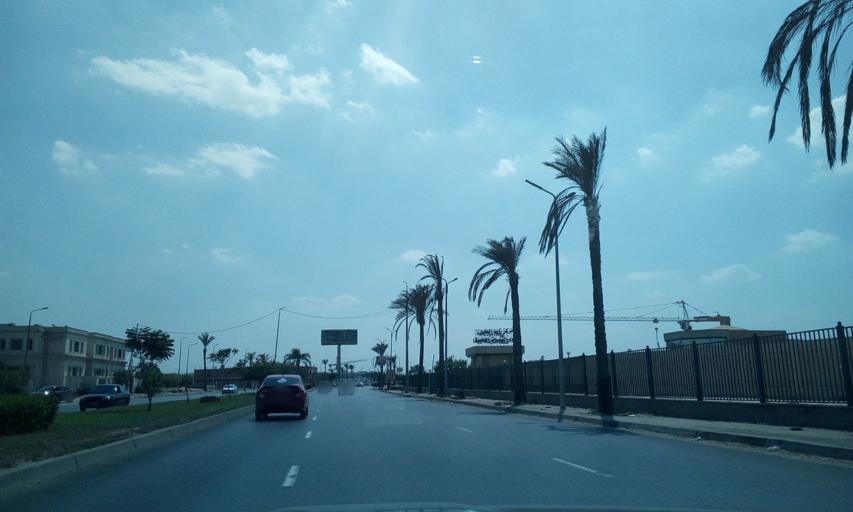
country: EG
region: Muhafazat al Qahirah
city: Cairo
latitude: 30.0878
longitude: 31.3676
